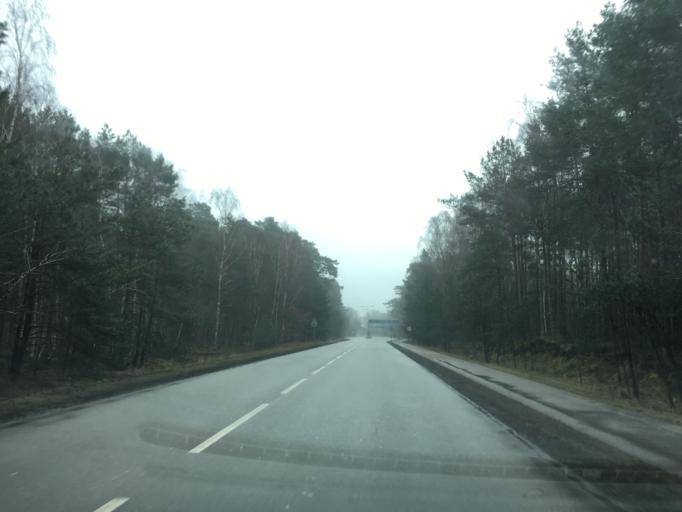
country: PL
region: West Pomeranian Voivodeship
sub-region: Swinoujscie
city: Swinoujscie
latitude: 53.8594
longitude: 14.2700
